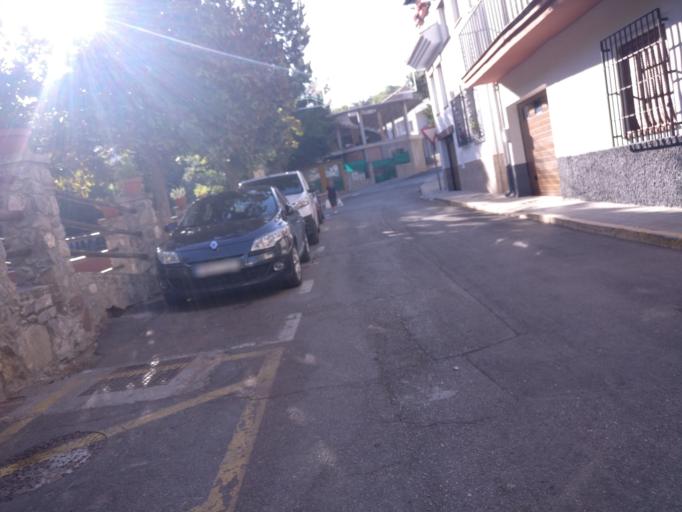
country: ES
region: Andalusia
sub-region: Provincia de Granada
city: Pinos Genil
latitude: 37.1635
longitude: -3.5019
